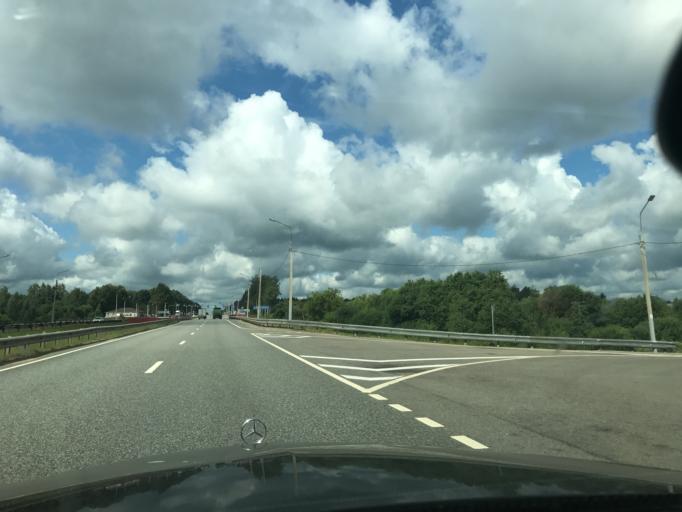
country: RU
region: Smolensk
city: Golynki
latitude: 54.7307
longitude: 31.3365
